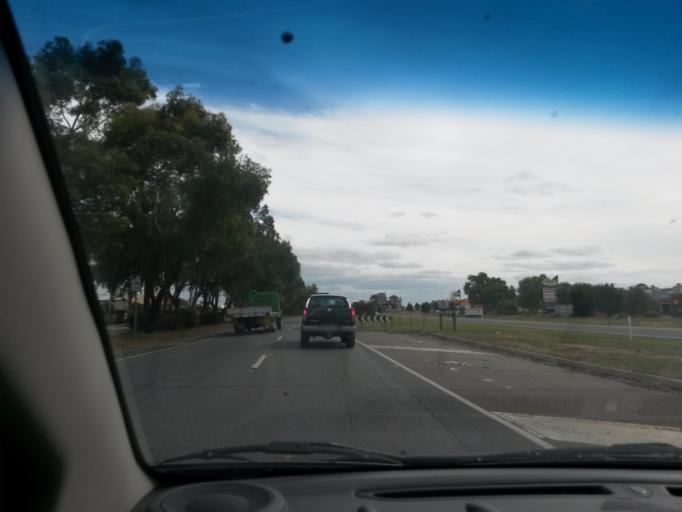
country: AU
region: South Australia
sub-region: Salisbury
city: Salisbury
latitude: -34.7940
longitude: 138.6451
